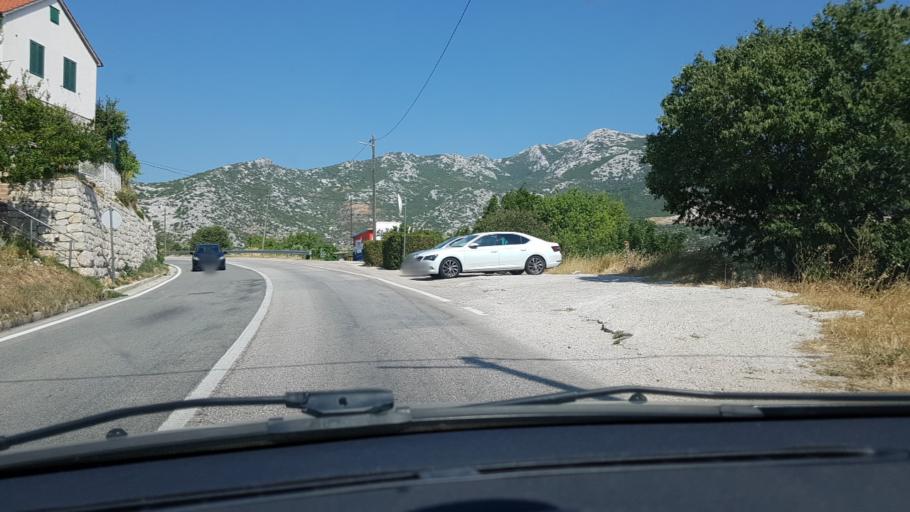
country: HR
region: Splitsko-Dalmatinska
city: Klis
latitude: 43.5579
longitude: 16.5236
